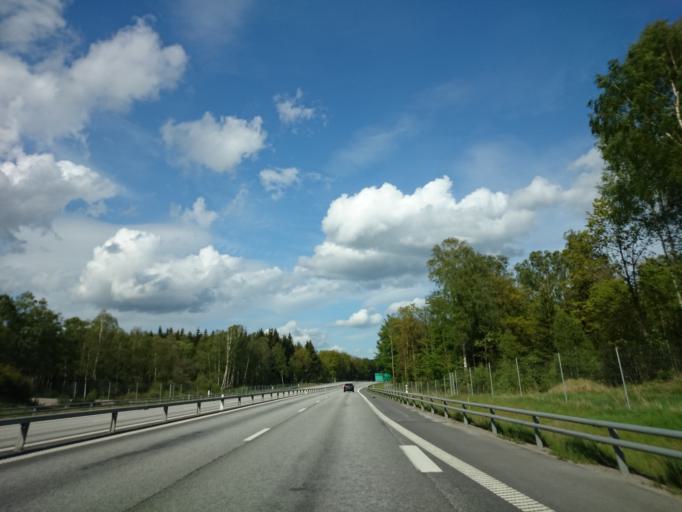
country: SE
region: Skane
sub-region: Horby Kommun
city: Hoerby
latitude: 55.9070
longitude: 13.7459
